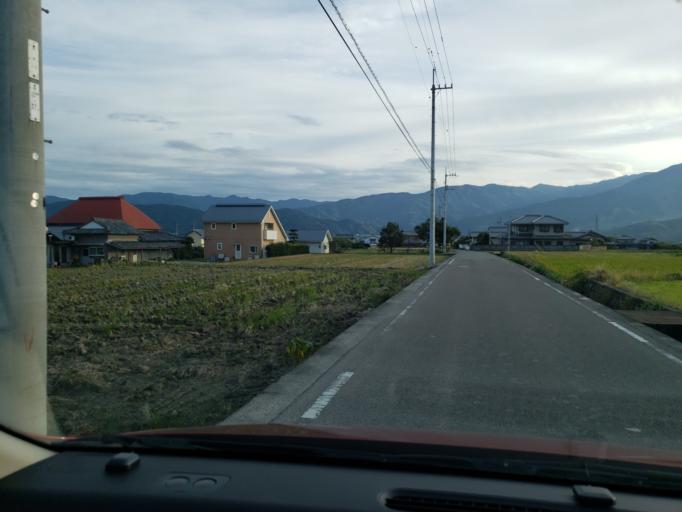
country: JP
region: Tokushima
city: Wakimachi
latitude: 34.0867
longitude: 134.2267
